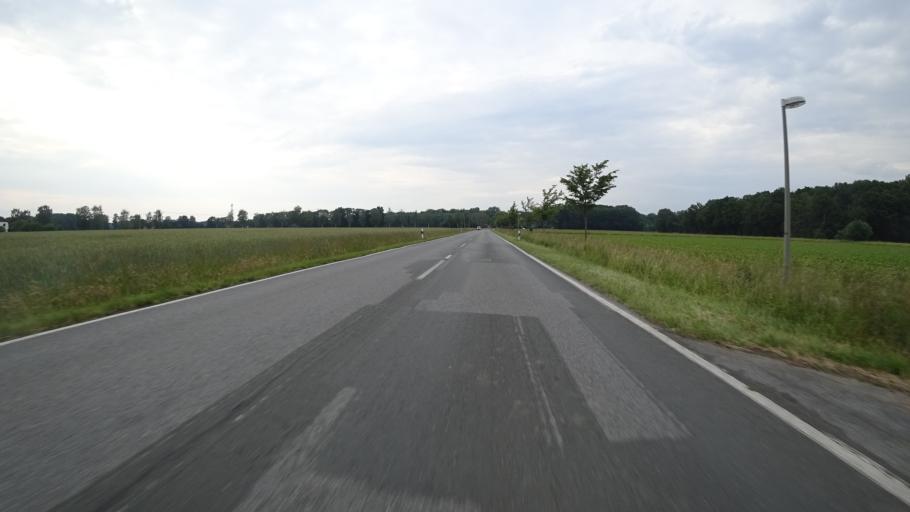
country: DE
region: North Rhine-Westphalia
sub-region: Regierungsbezirk Detmold
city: Guetersloh
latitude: 51.9379
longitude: 8.3798
